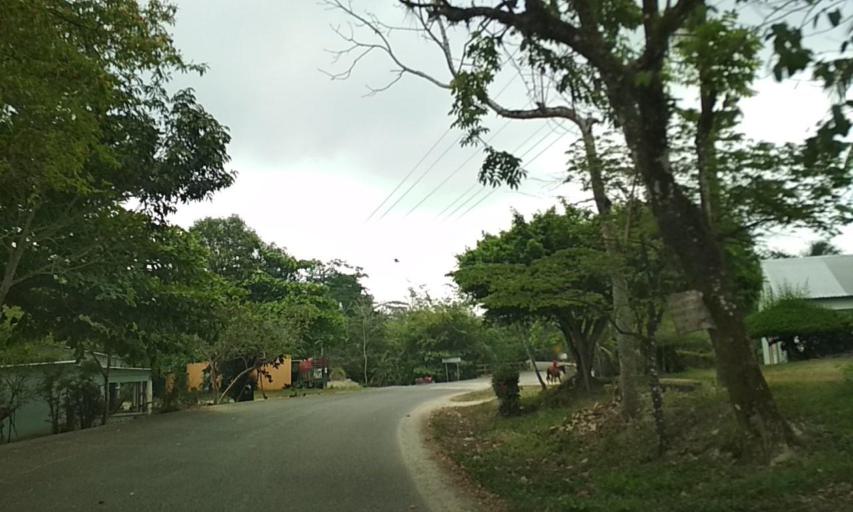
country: MX
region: Tabasco
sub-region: Huimanguillo
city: Francisco Rueda
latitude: 17.5787
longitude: -94.0976
